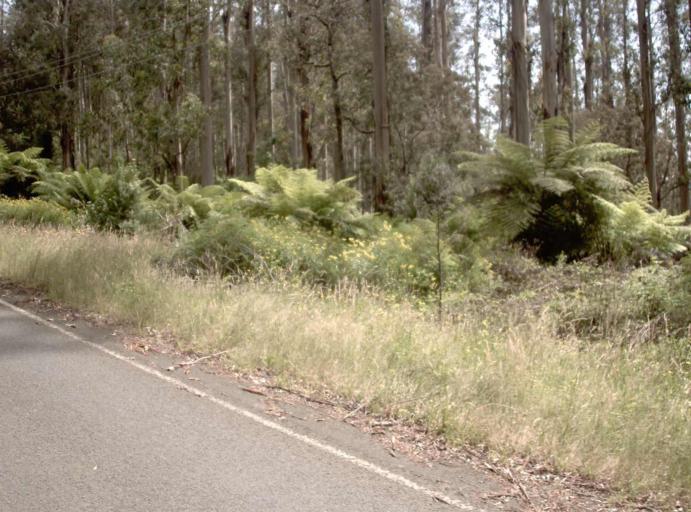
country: AU
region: Victoria
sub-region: Latrobe
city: Moe
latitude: -37.8798
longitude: 146.3796
